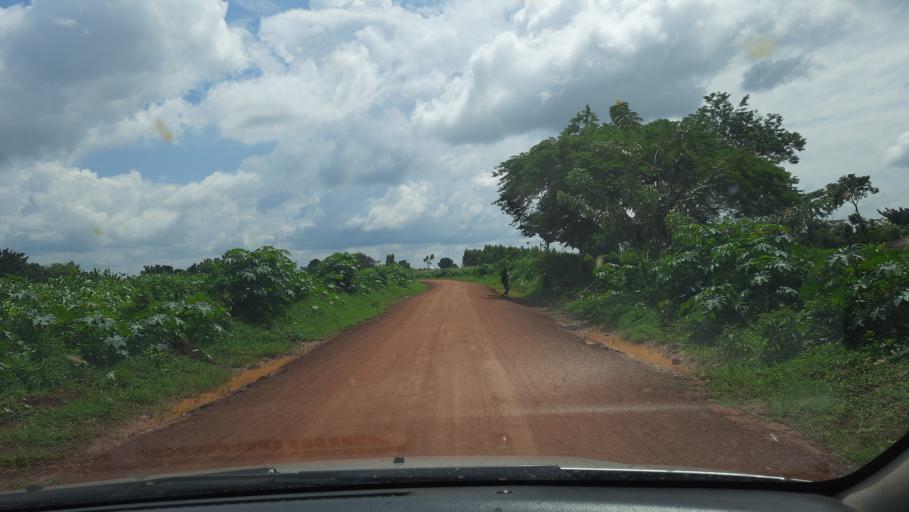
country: UG
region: Western Region
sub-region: Kiryandongo District
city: Kiryandongo
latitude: 1.8226
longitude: 31.9832
